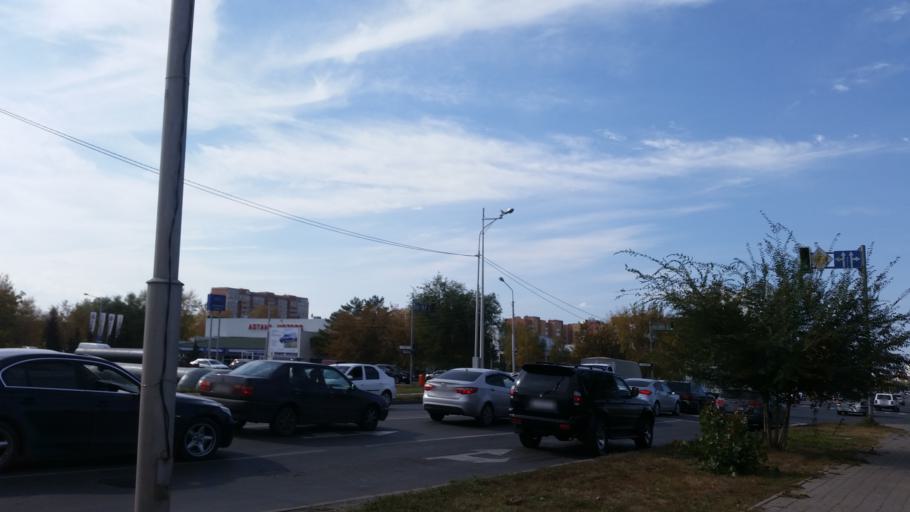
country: KZ
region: Astana Qalasy
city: Astana
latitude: 51.1623
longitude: 71.4841
